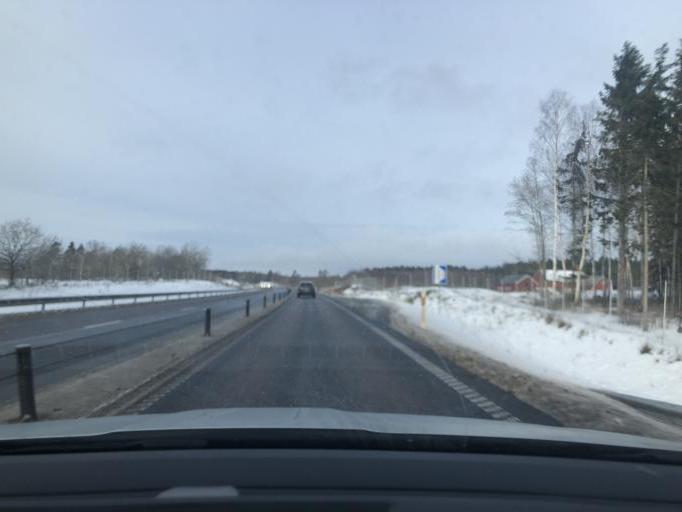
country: SE
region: OEstergoetland
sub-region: Motala Kommun
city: Borensberg
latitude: 58.5877
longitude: 15.1891
